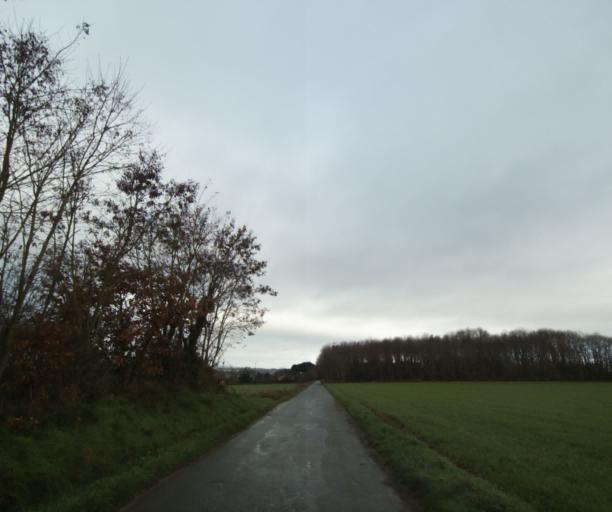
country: FR
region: Pays de la Loire
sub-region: Departement de la Sarthe
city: Rouillon
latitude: 48.0222
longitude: 0.1434
